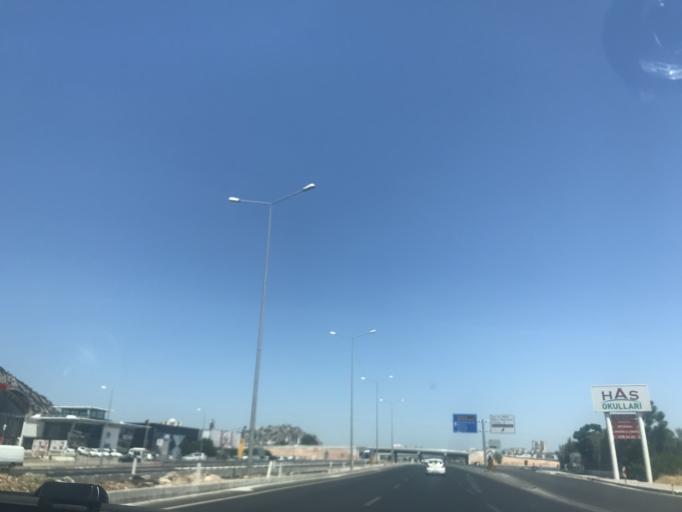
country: TR
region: Antalya
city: Cakirlar
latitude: 36.8436
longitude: 30.5989
